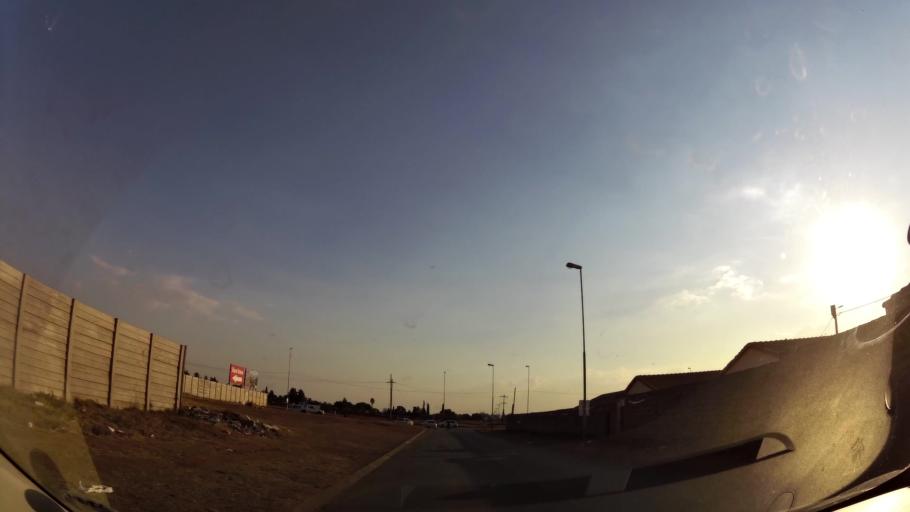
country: ZA
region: Gauteng
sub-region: Ekurhuleni Metropolitan Municipality
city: Boksburg
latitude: -26.2937
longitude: 28.2531
